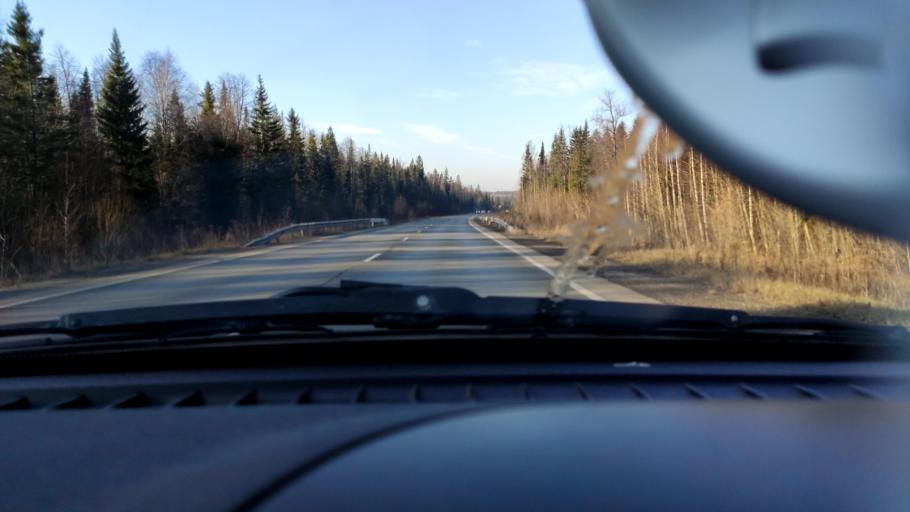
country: RU
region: Perm
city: Novyye Lyady
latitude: 58.0303
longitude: 56.4890
